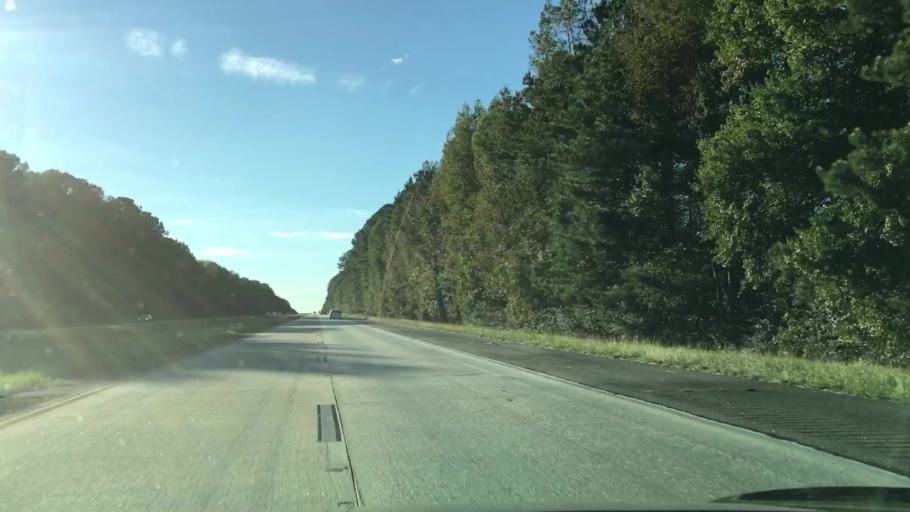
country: US
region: Georgia
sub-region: Greene County
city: Union Point
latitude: 33.5474
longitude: -83.1057
